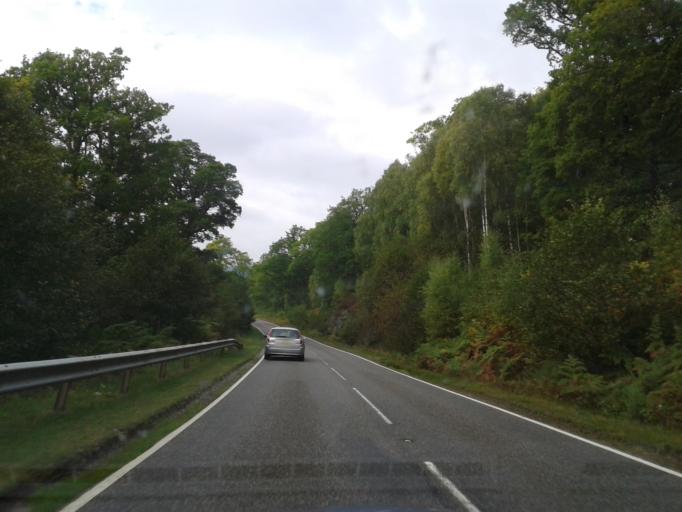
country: GB
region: Scotland
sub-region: Highland
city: Spean Bridge
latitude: 57.0818
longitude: -4.8849
